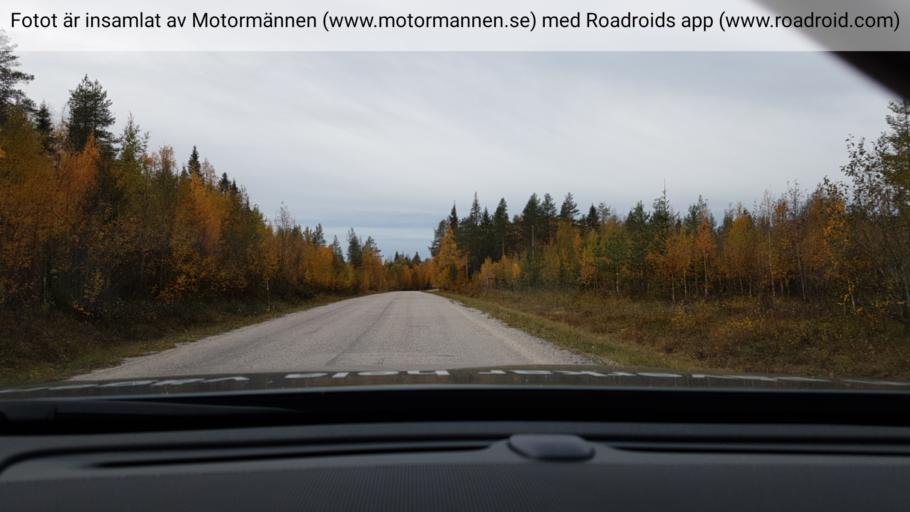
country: SE
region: Norrbotten
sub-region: Overkalix Kommun
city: OEverkalix
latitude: 66.2578
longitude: 23.0775
